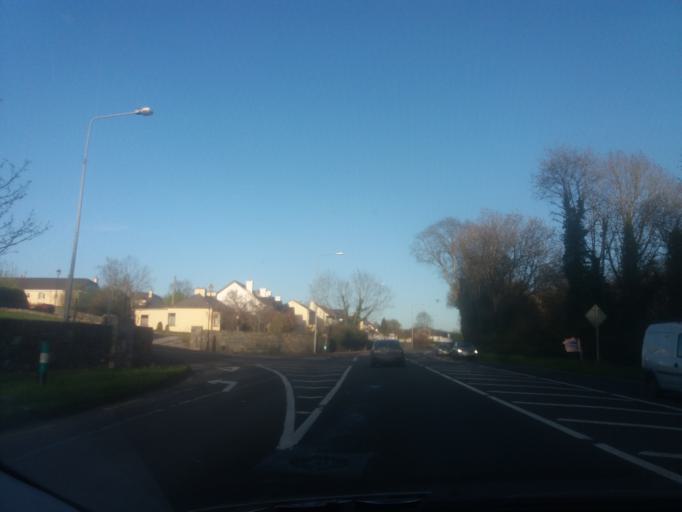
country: IE
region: Munster
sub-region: Ciarrai
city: Cill Airne
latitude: 52.0686
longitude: -9.5317
